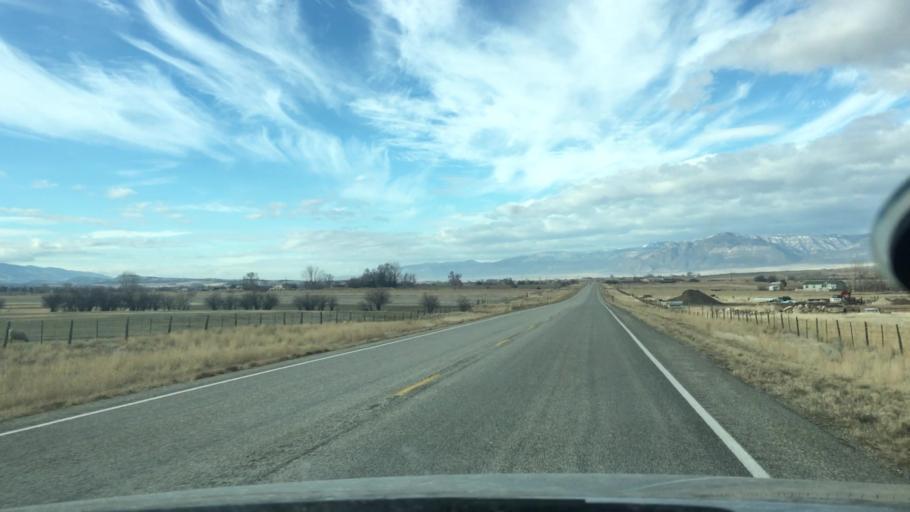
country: US
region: Utah
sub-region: Sanpete County
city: Mount Pleasant
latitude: 39.5207
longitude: -111.4826
